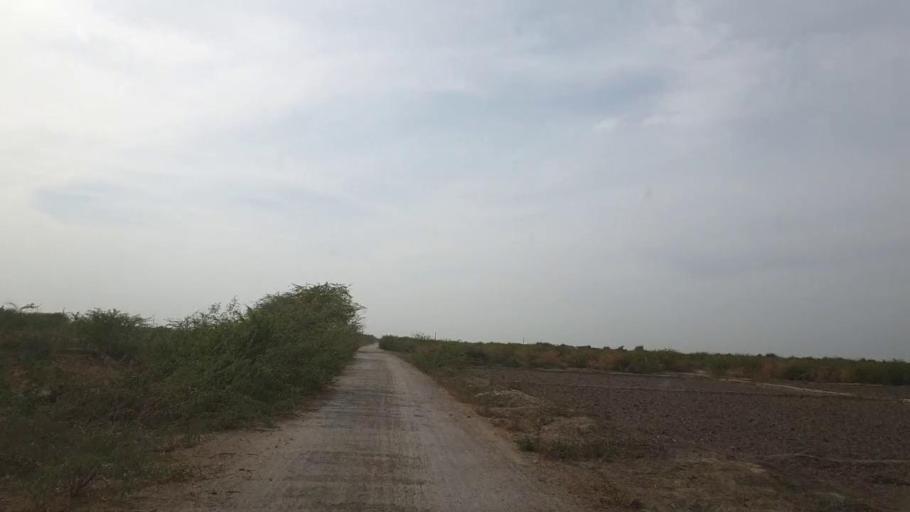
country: PK
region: Sindh
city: Nabisar
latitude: 24.9944
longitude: 69.5549
